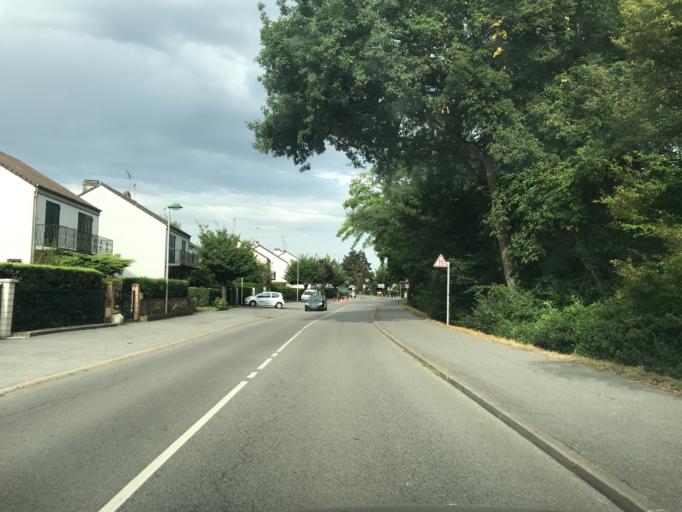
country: FR
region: Ile-de-France
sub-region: Departement des Yvelines
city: Maurepas
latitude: 48.7672
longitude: 1.9357
